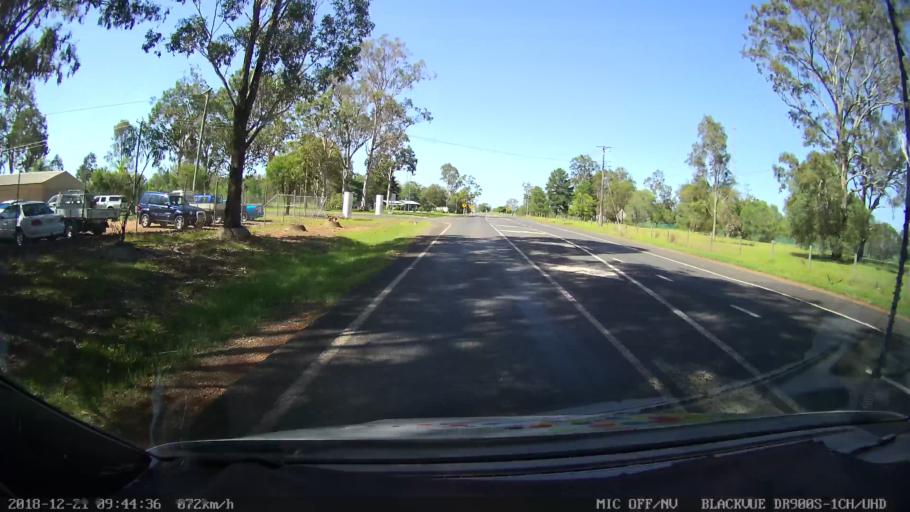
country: AU
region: New South Wales
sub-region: Clarence Valley
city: Grafton
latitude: -29.6198
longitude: 152.9326
